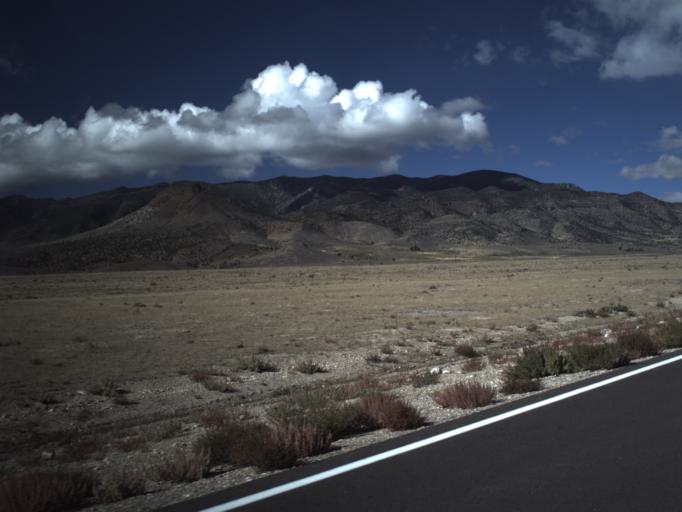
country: US
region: Utah
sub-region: Beaver County
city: Milford
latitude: 38.4873
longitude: -113.4586
